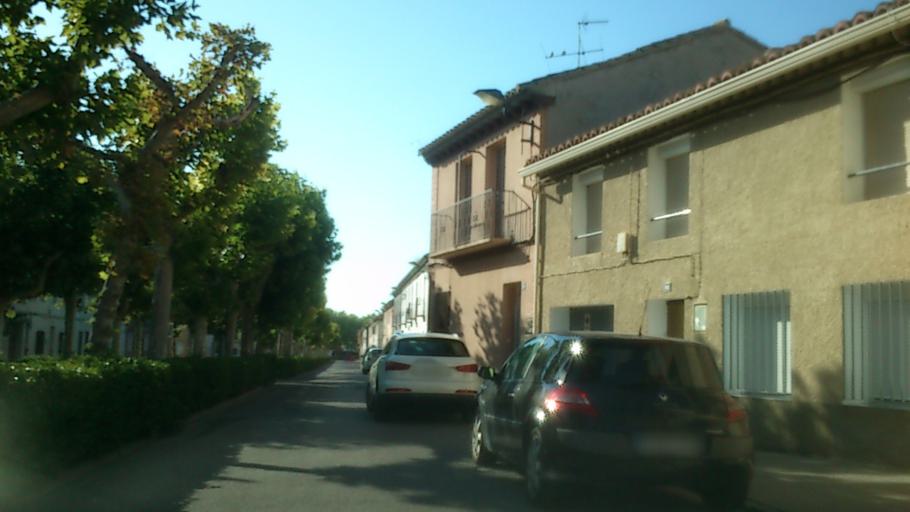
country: ES
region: Aragon
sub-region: Provincia de Zaragoza
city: Villanueva de Gallego
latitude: 41.7672
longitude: -0.8250
